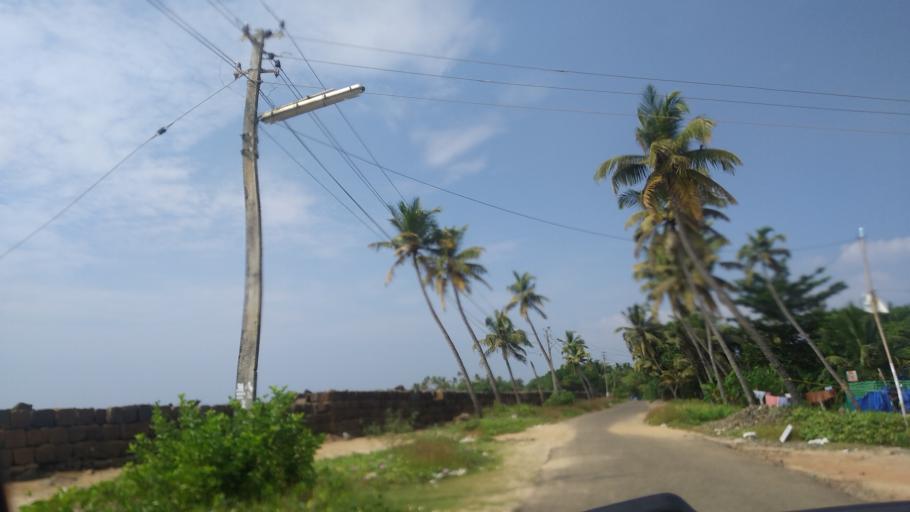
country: IN
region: Kerala
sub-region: Ernakulam
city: Elur
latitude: 10.0491
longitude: 76.2048
